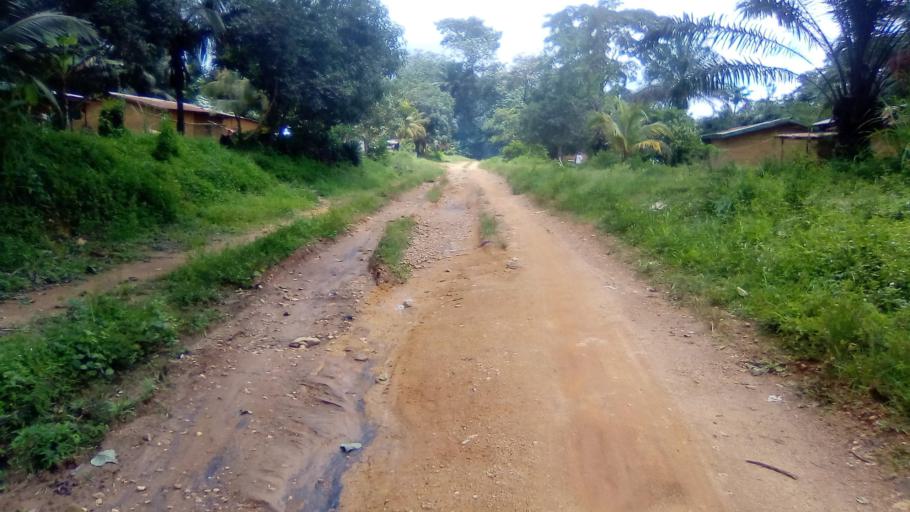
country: SL
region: Eastern Province
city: Simbakoro
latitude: 8.5230
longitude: -10.9088
